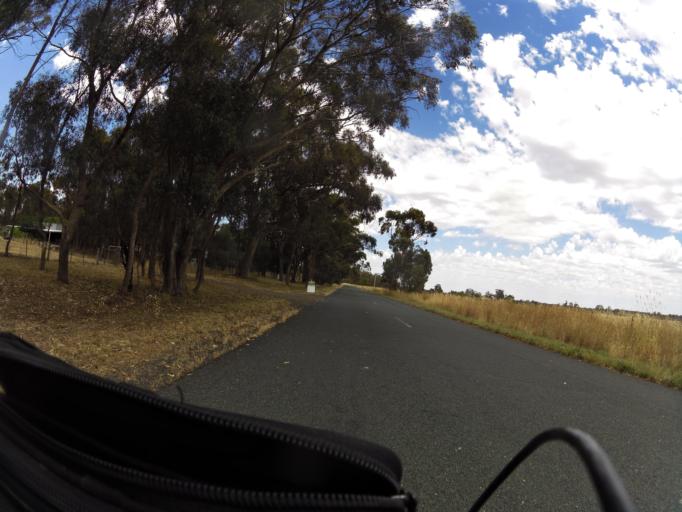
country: AU
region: Victoria
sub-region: Greater Shepparton
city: Shepparton
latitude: -36.6648
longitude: 145.1992
